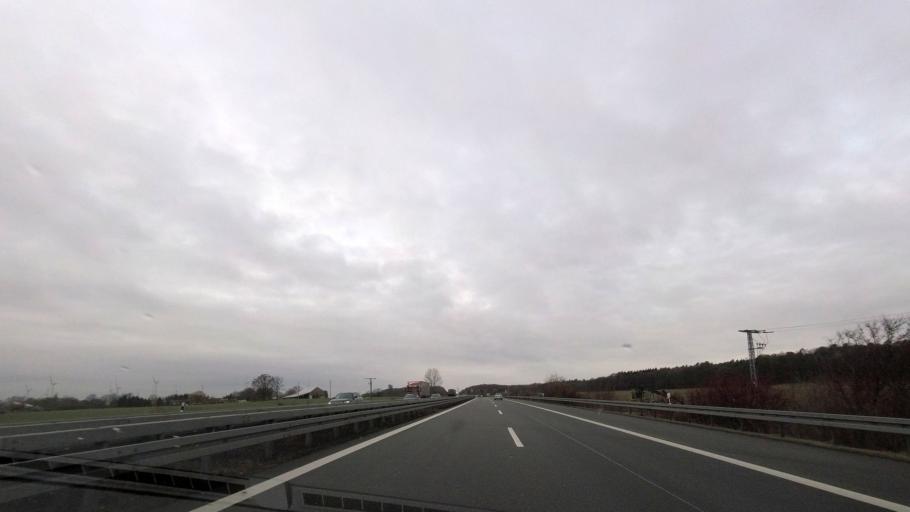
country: DE
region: Brandenburg
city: Gerdshagen
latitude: 53.2507
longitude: 12.1736
